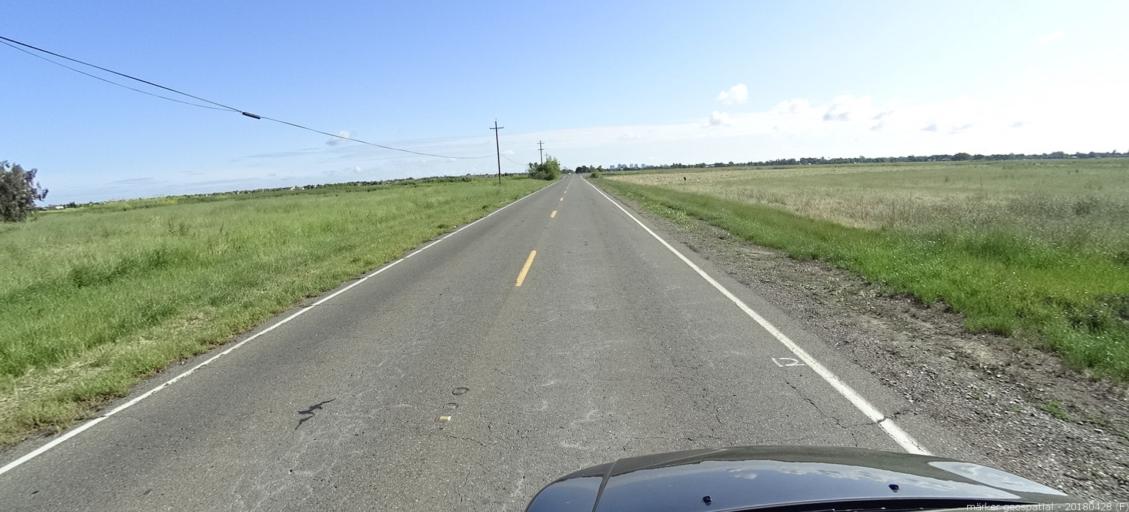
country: US
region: California
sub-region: Yolo County
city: West Sacramento
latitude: 38.5145
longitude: -121.5729
